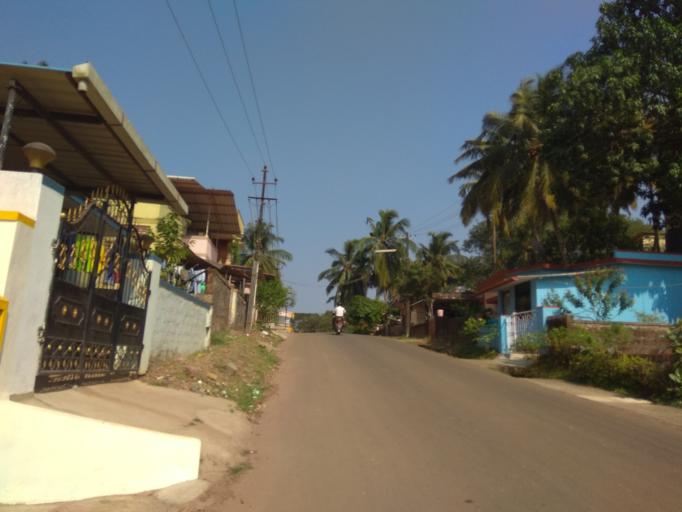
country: IN
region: Karnataka
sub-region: Dakshina Kannada
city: Mangalore
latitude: 12.9410
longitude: 74.8527
